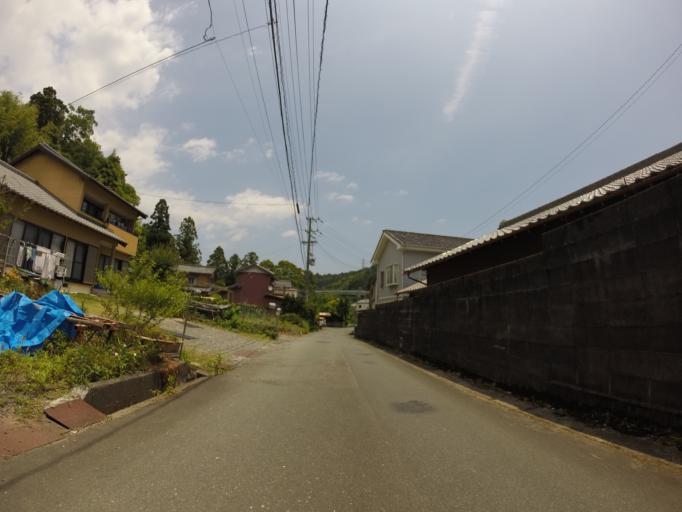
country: JP
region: Shizuoka
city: Kanaya
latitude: 34.8048
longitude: 138.0734
